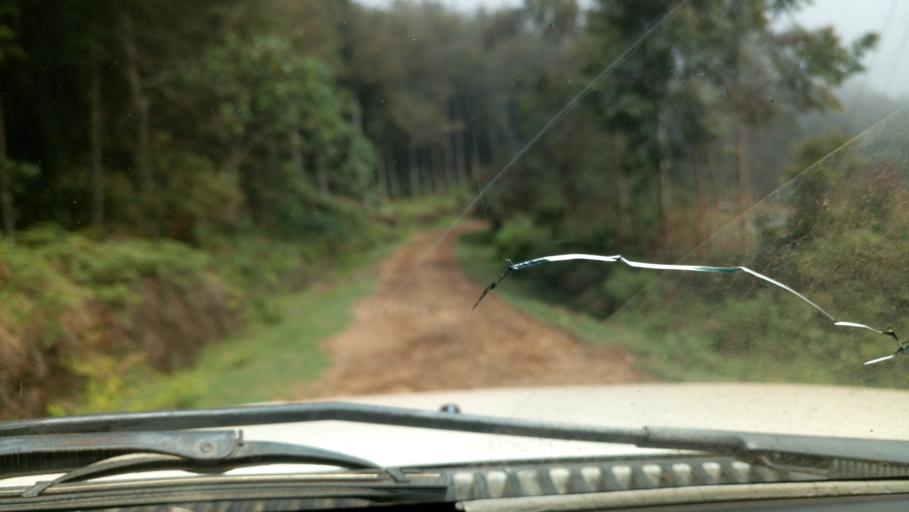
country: KE
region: Murang'a District
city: Kangema
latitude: -0.6561
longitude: 36.8355
